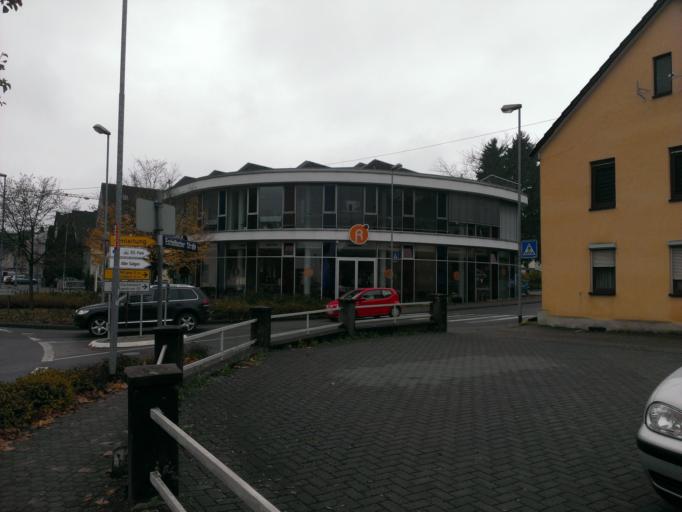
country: DE
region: Rheinland-Pfalz
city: Montabaur
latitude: 50.4406
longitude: 7.8252
